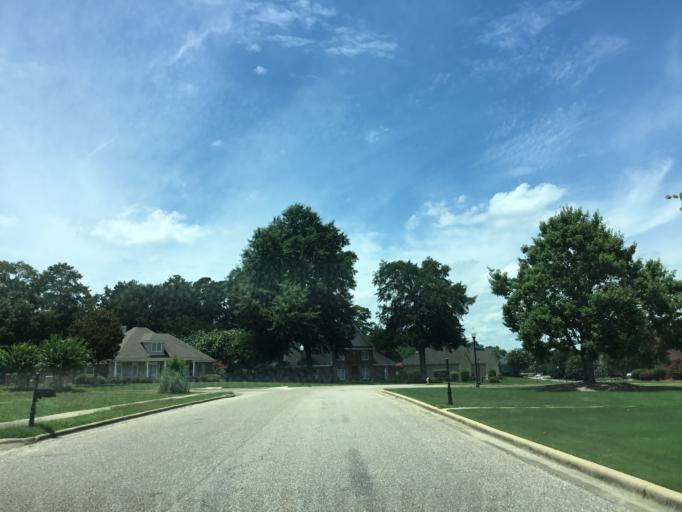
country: US
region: Alabama
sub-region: Montgomery County
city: Pike Road
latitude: 32.3795
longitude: -86.1359
